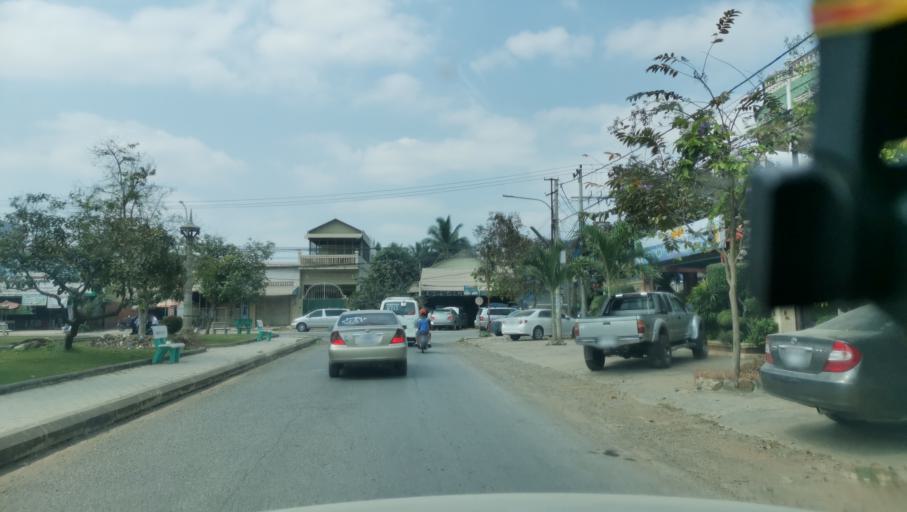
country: KH
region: Battambang
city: Battambang
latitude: 13.1081
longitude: 103.1960
